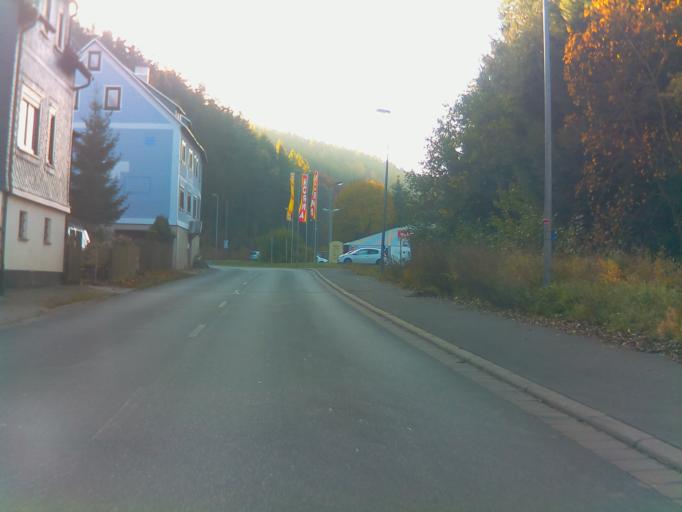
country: DE
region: Thuringia
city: Piesau
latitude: 50.5225
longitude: 11.2232
